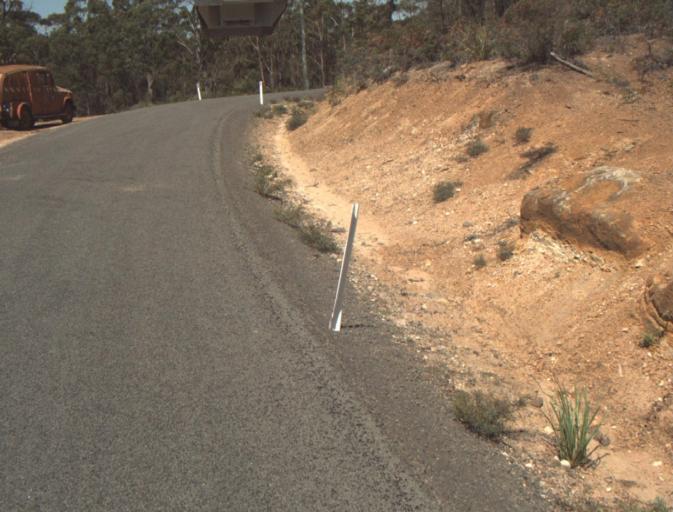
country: AU
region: Tasmania
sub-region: Launceston
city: Mayfield
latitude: -41.3191
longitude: 147.1223
